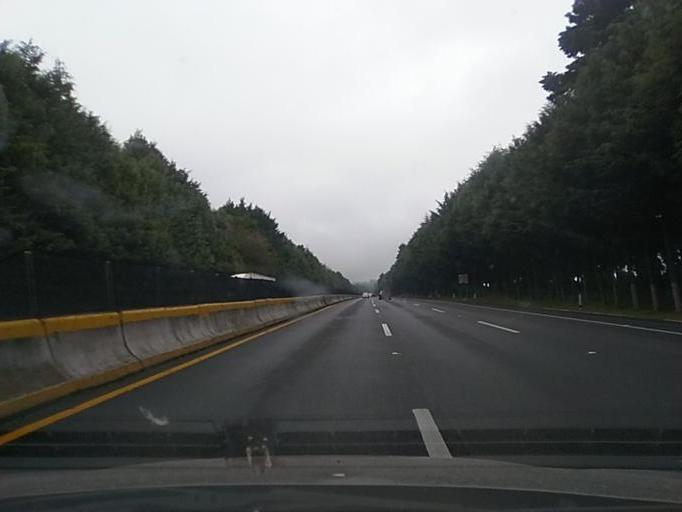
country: MX
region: Mexico City
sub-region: Tlalpan
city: Lomas de Tepemecatl
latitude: 19.1473
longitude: -99.1611
